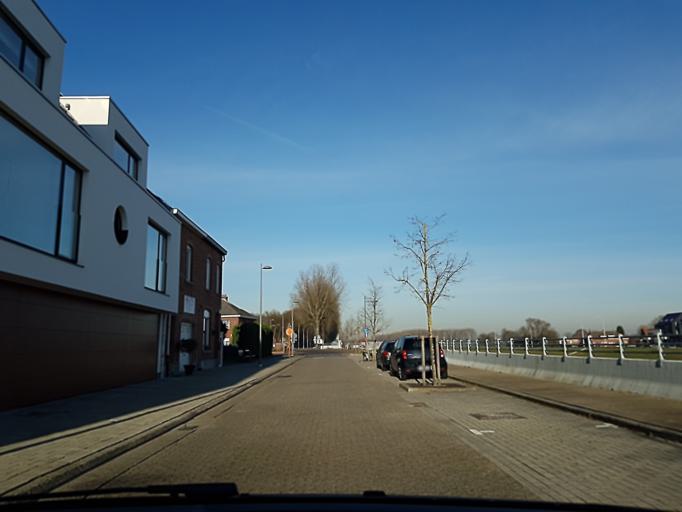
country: BE
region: Flanders
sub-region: Provincie Vlaams-Brabant
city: Kapelle-op-den-Bos
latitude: 51.0137
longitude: 4.3634
